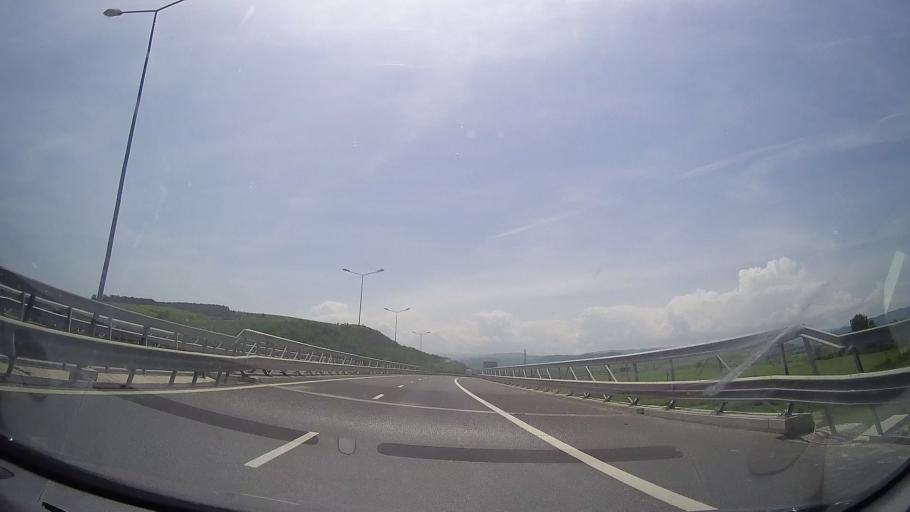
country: RO
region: Alba
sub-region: Municipiul Sebes
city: Sebes
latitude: 45.9657
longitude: 23.5955
